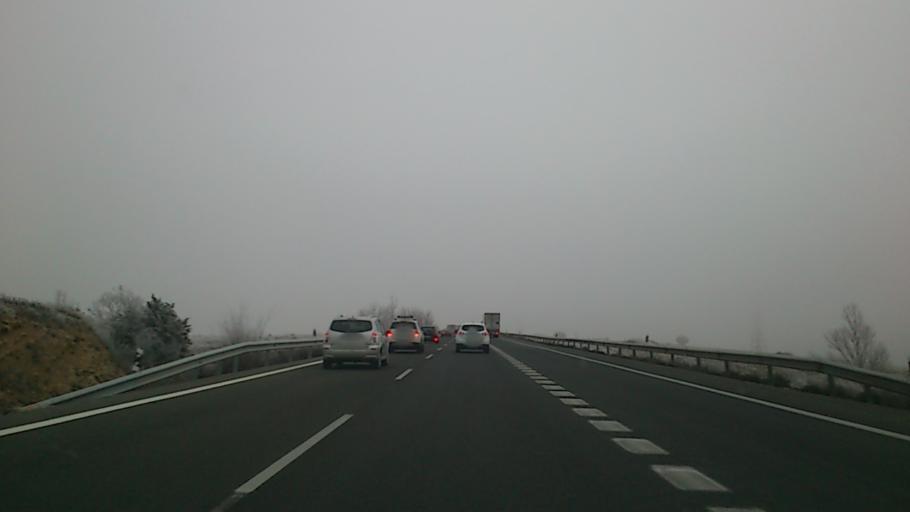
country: ES
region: Castille-La Mancha
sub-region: Provincia de Guadalajara
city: Torremocha del Campo
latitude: 40.9891
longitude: -2.5990
